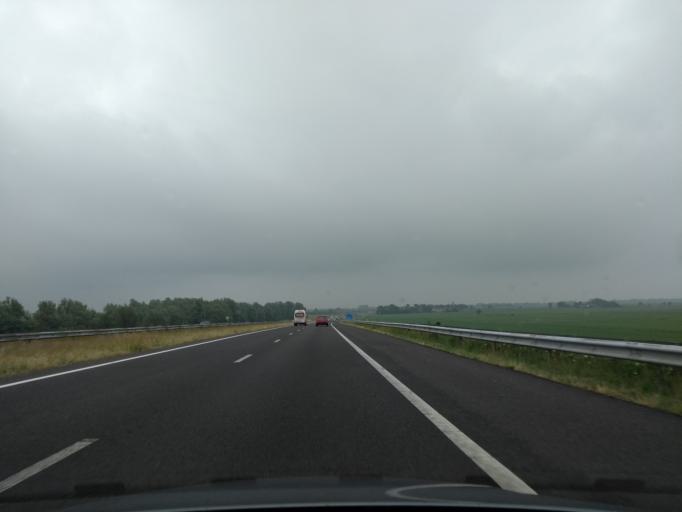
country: NL
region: Friesland
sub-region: Gemeente Skarsterlan
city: Joure
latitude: 52.9724
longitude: 5.7579
